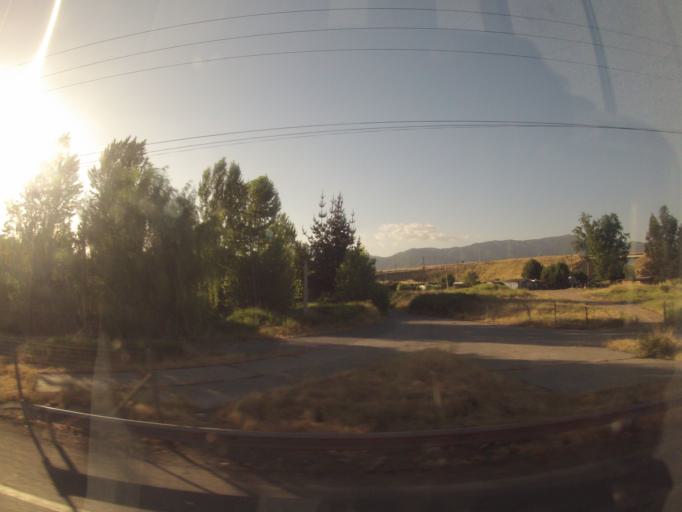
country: CL
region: O'Higgins
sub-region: Provincia de Colchagua
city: Chimbarongo
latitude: -34.6079
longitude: -70.9850
